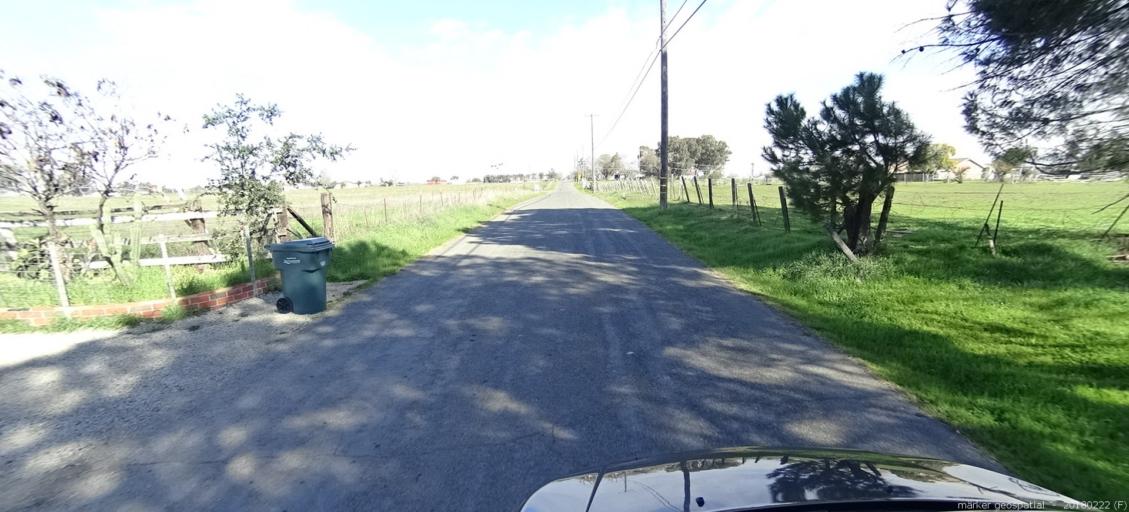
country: US
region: California
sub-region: Sacramento County
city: Elverta
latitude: 38.7217
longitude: -121.4435
